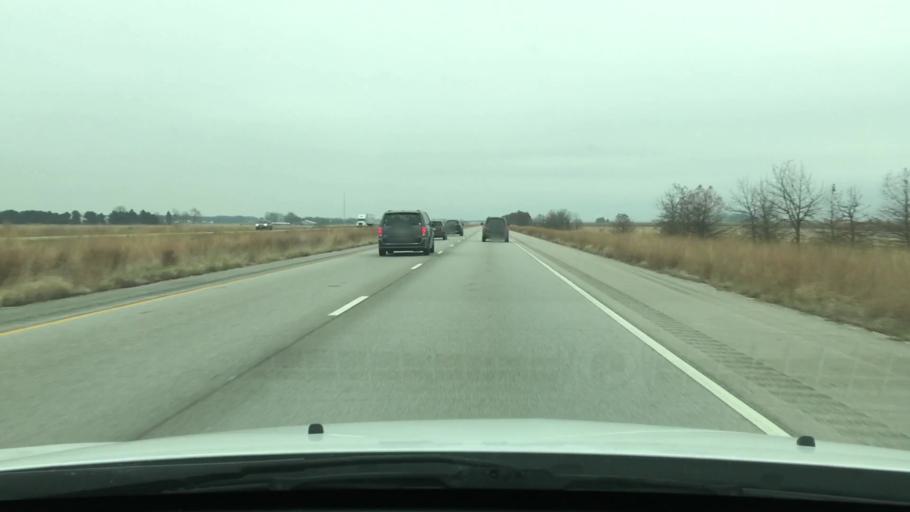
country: US
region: Illinois
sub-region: Sangamon County
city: New Berlin
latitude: 39.7368
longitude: -90.0108
